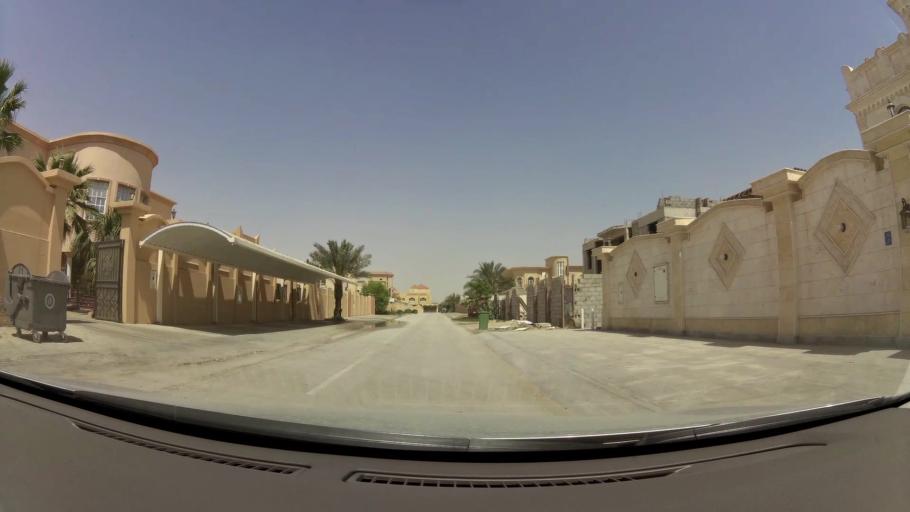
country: QA
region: Baladiyat ar Rayyan
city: Ar Rayyan
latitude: 25.3631
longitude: 51.4784
